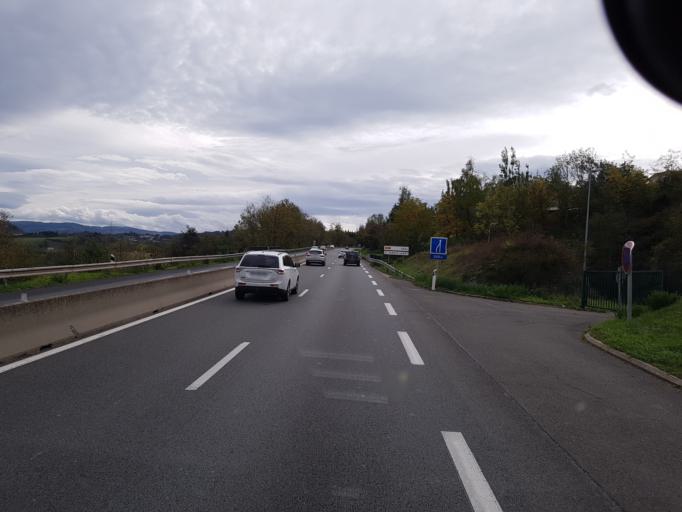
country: FR
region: Rhone-Alpes
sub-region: Departement de la Loire
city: Saint-Genest-Lerpt
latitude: 45.4458
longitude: 4.3390
